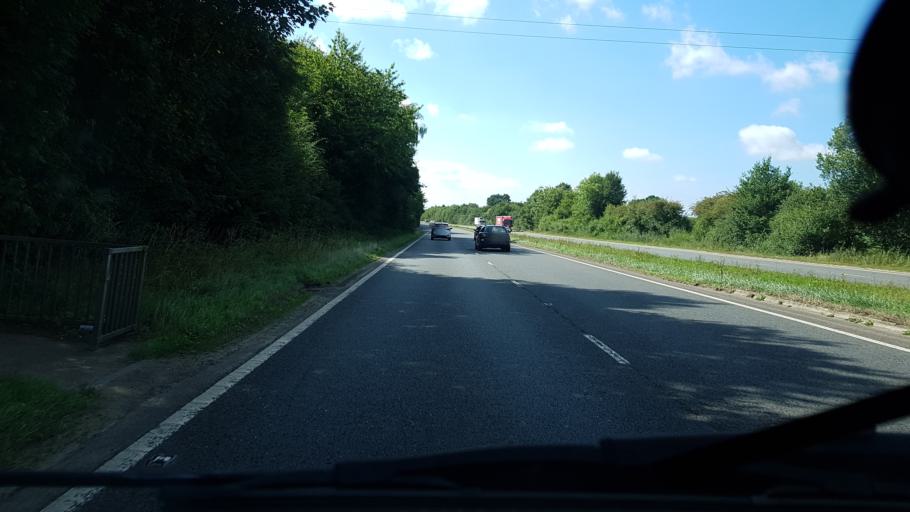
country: GB
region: England
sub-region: West Sussex
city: Horsham
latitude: 51.0884
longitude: -0.3120
